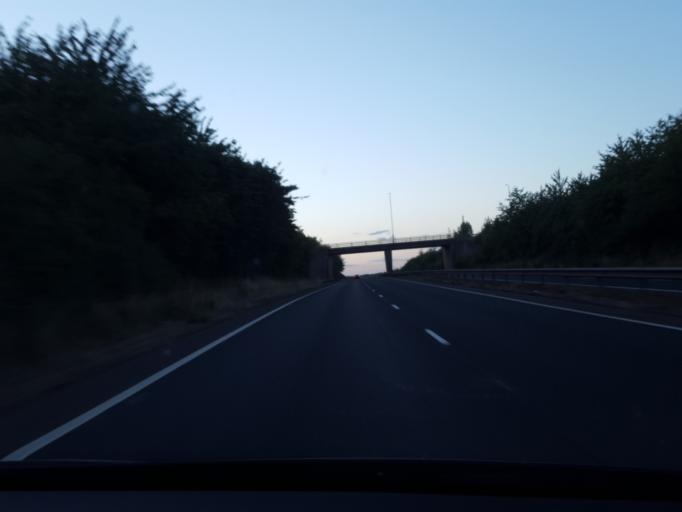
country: GB
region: England
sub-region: Leicestershire
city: Mountsorrel
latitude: 52.7180
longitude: -1.1273
